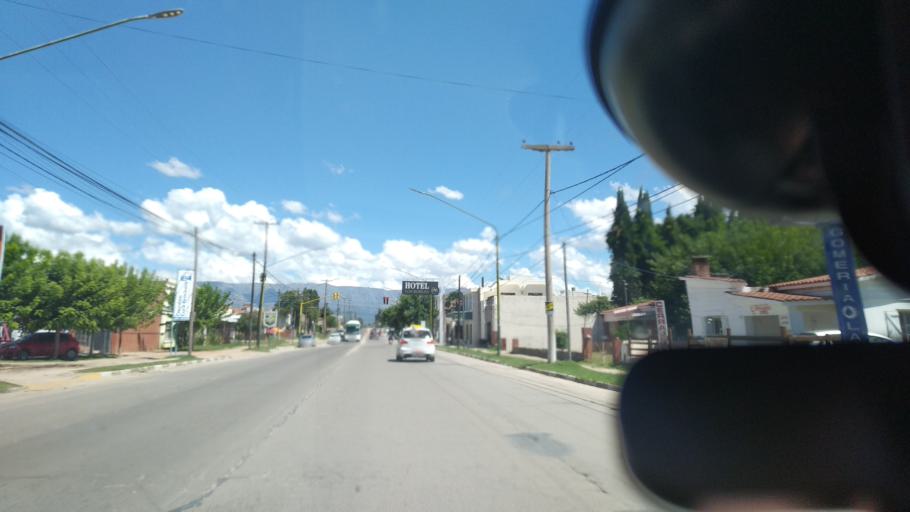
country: AR
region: Cordoba
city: Villa Cura Brochero
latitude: -31.7138
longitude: -65.0139
